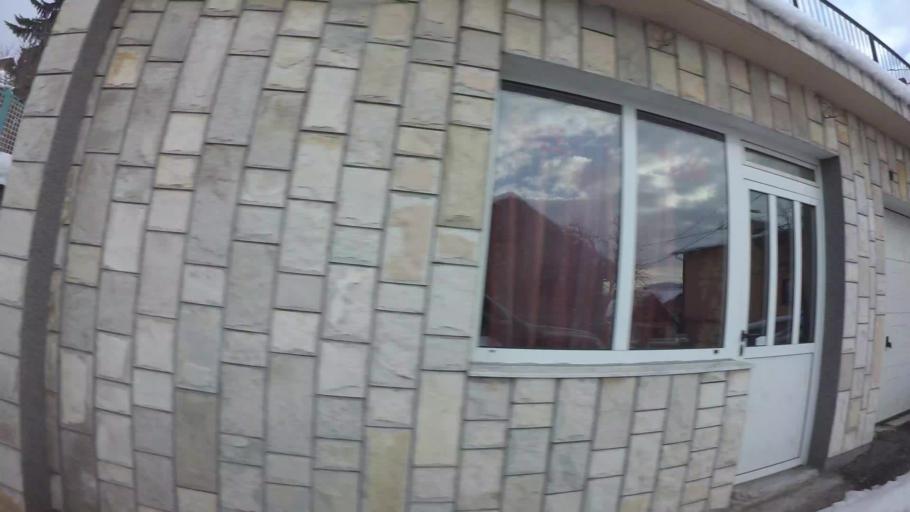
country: BA
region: Federation of Bosnia and Herzegovina
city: Kobilja Glava
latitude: 43.8614
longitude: 18.3777
